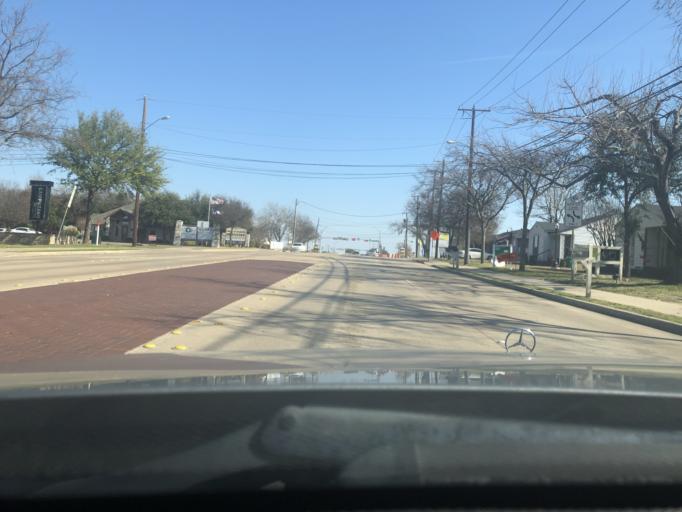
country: US
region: Texas
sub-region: Dallas County
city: Cedar Hill
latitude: 32.5900
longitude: -96.9490
